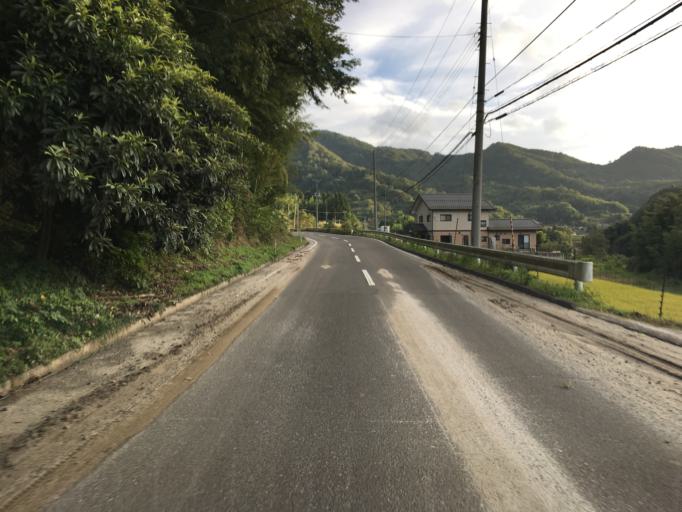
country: JP
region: Fukushima
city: Yanagawamachi-saiwaicho
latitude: 37.9058
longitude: 140.6630
